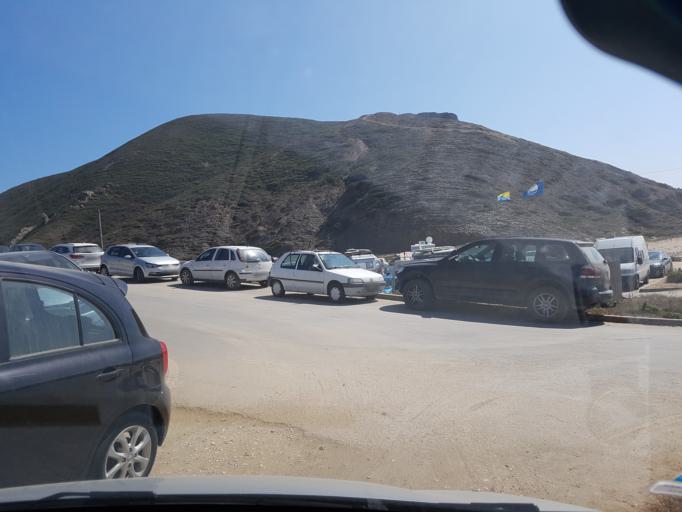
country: PT
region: Faro
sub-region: Vila do Bispo
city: Vila do Bispo
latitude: 37.1093
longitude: -8.9356
